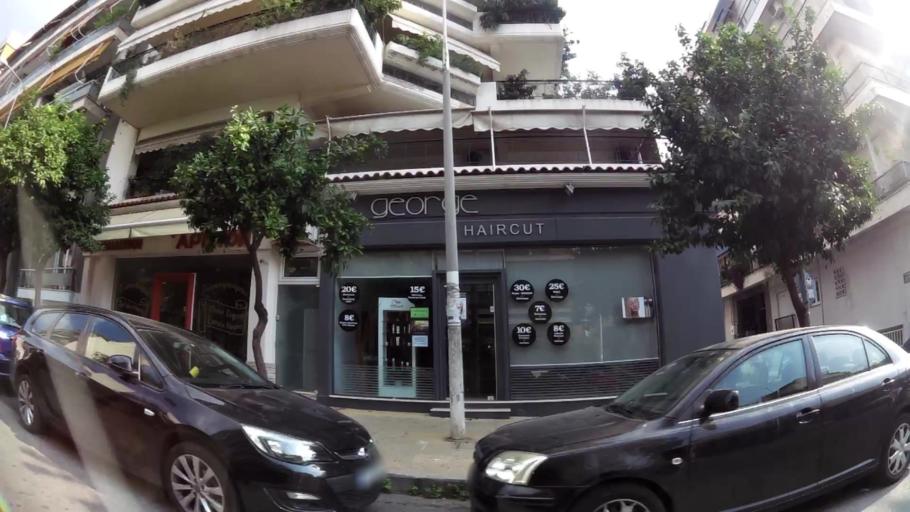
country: GR
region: Attica
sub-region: Nomarchia Athinas
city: Nea Smyrni
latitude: 37.9565
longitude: 23.7108
